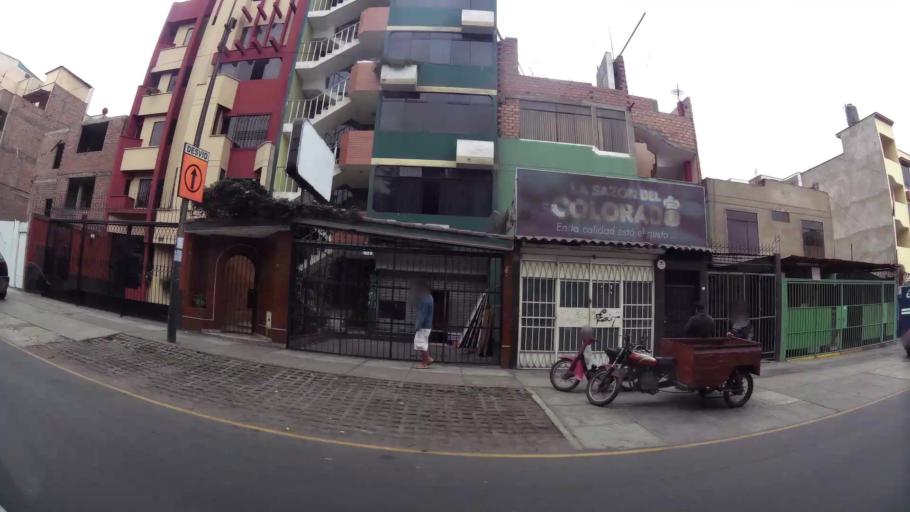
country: PE
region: Lima
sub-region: Lima
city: Surco
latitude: -12.1454
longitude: -76.9854
